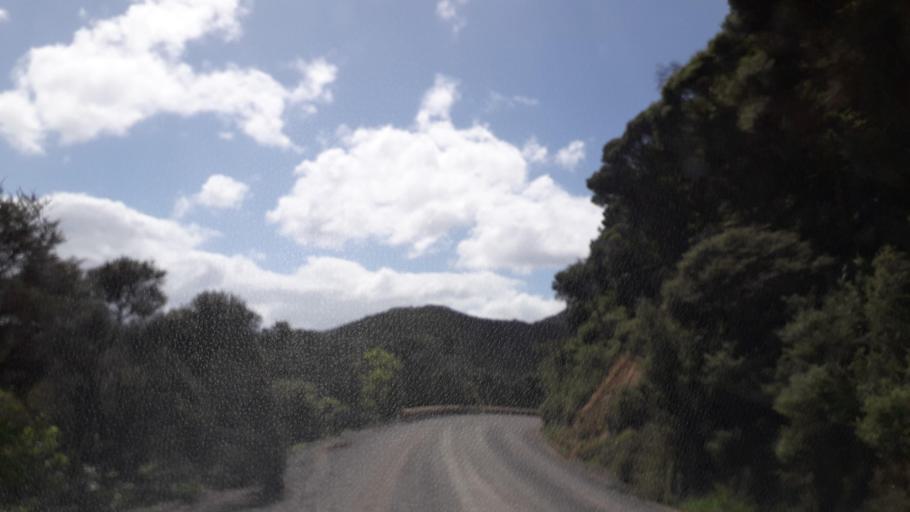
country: NZ
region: Northland
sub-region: Far North District
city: Paihia
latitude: -35.2607
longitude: 174.2643
